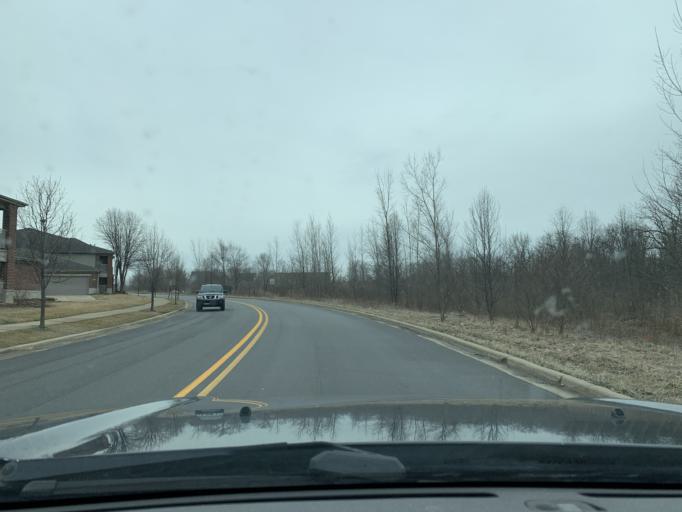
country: US
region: Indiana
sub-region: Porter County
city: Chesterton
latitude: 41.5890
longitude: -87.0367
